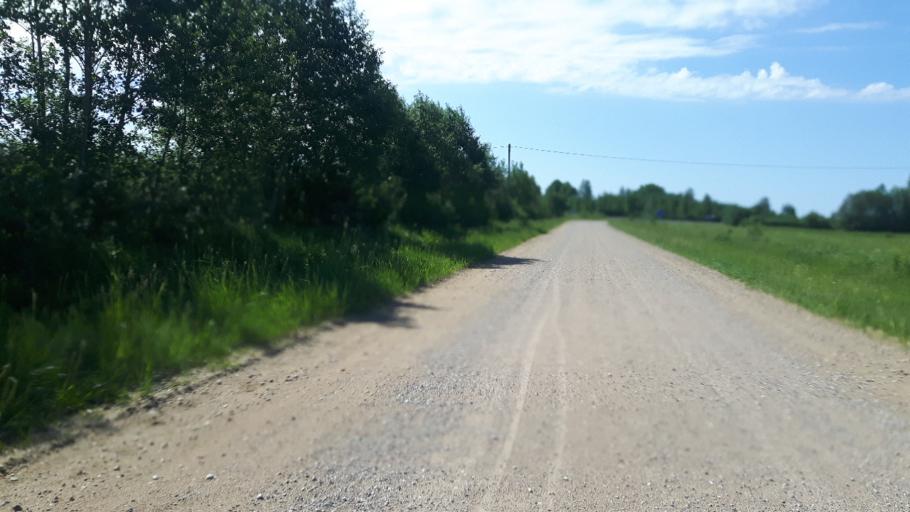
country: EE
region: Paernumaa
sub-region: Vaendra vald (alev)
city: Vandra
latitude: 58.6648
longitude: 25.0249
